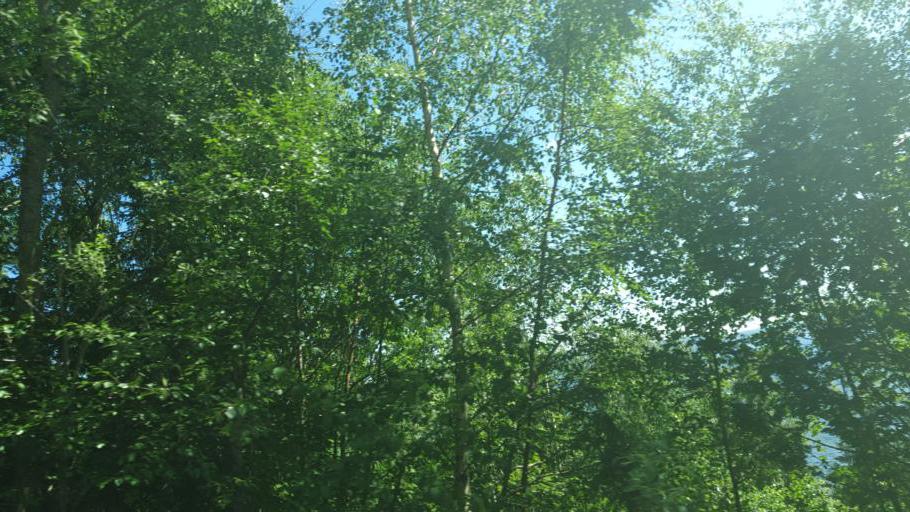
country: NO
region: Nord-Trondelag
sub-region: Frosta
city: Frosta
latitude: 63.7093
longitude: 10.7724
